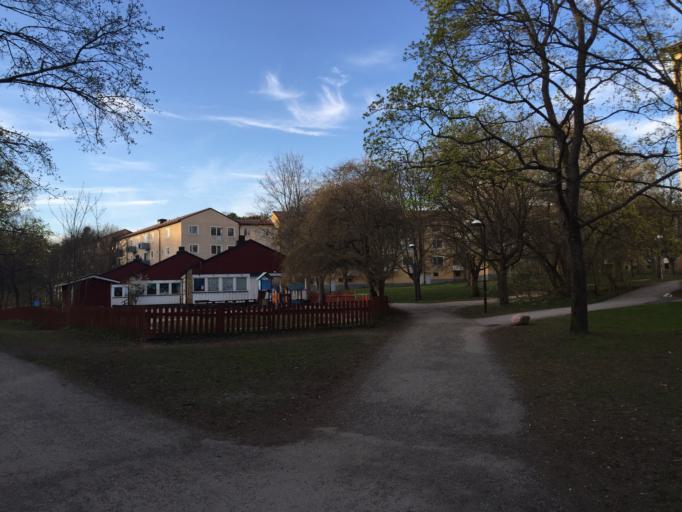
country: SE
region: Stockholm
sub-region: Stockholms Kommun
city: Bromma
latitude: 59.3576
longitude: 17.8859
